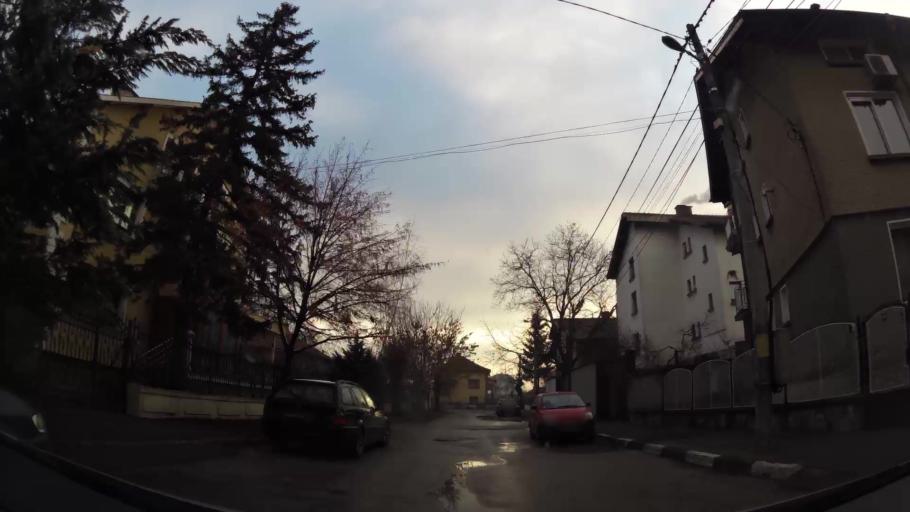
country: BG
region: Sofia-Capital
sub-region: Stolichna Obshtina
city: Sofia
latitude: 42.7358
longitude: 23.3462
